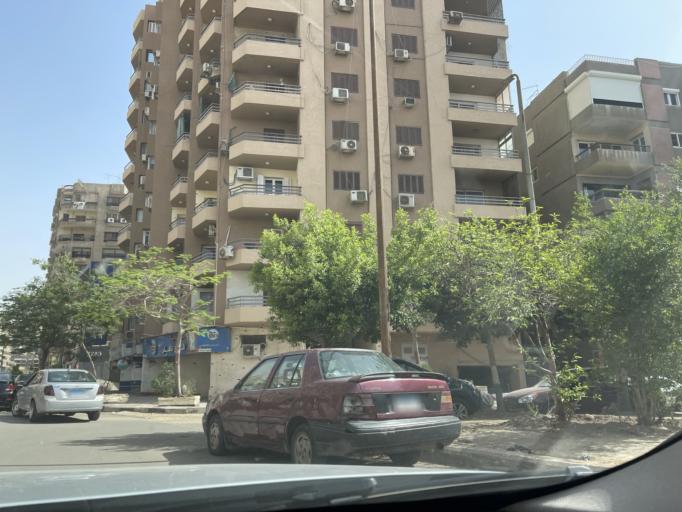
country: EG
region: Muhafazat al Qahirah
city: Cairo
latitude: 30.0689
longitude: 31.3549
